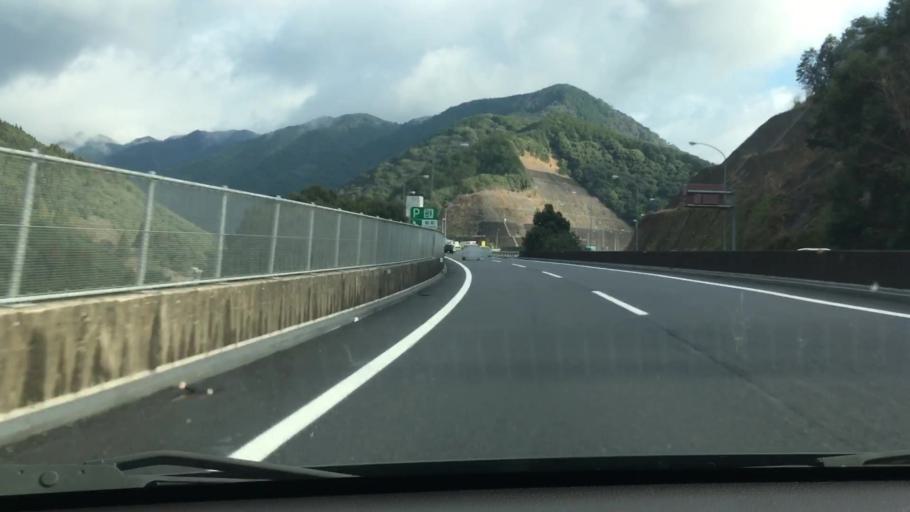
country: JP
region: Kumamoto
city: Yatsushiro
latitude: 32.4434
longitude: 130.6657
